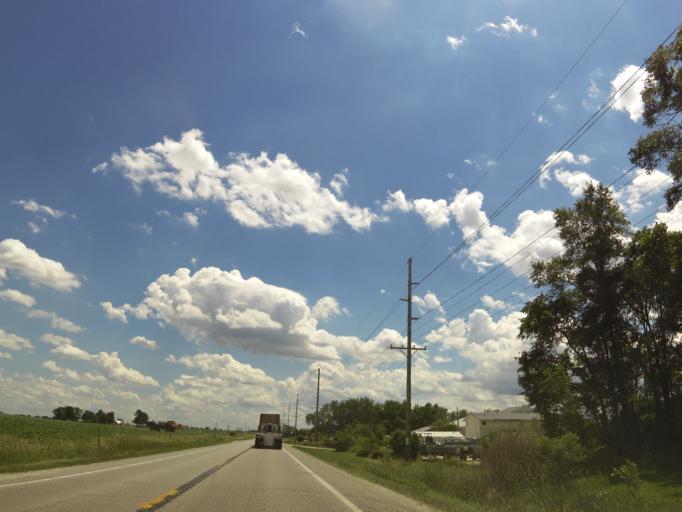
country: US
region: Iowa
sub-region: Buchanan County
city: Independence
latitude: 42.3771
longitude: -91.8894
